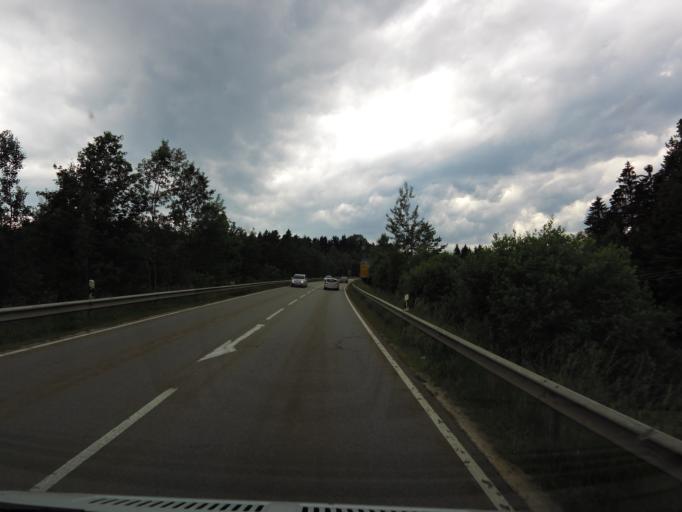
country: DE
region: Bavaria
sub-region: Lower Bavaria
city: Neukirchen vorm Wald
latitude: 48.6940
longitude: 13.3950
